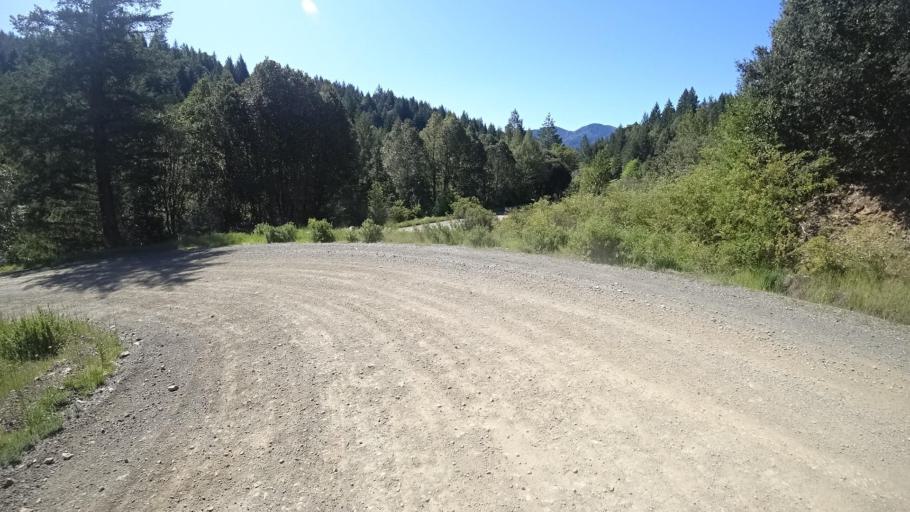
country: US
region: California
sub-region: Humboldt County
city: Rio Dell
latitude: 40.2266
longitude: -124.1103
